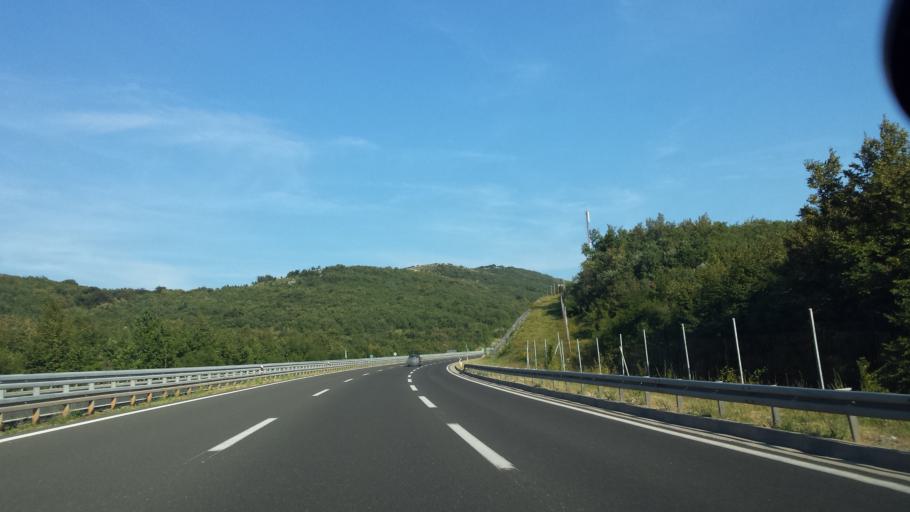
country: HR
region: Primorsko-Goranska
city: Krasica
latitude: 45.3617
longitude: 14.5717
